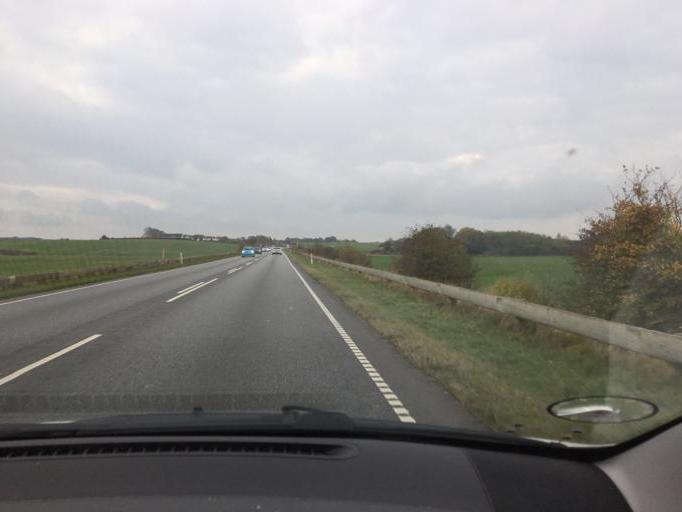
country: DK
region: South Denmark
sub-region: Fredericia Kommune
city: Fredericia
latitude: 55.6128
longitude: 9.7517
